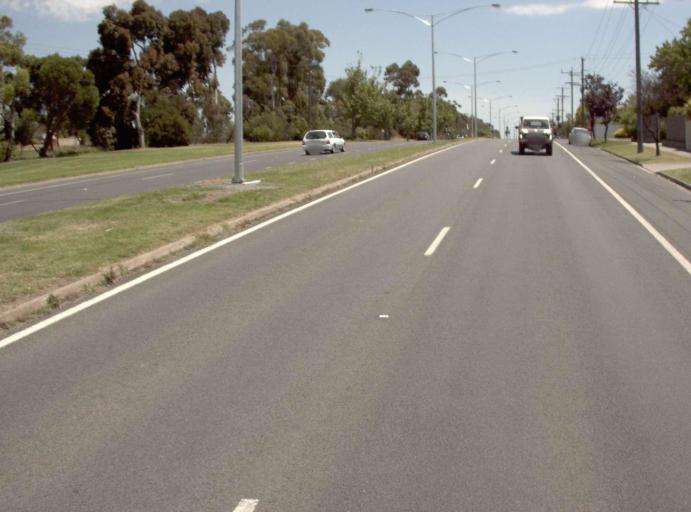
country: AU
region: Victoria
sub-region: Latrobe
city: Traralgon
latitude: -38.2014
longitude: 146.5259
